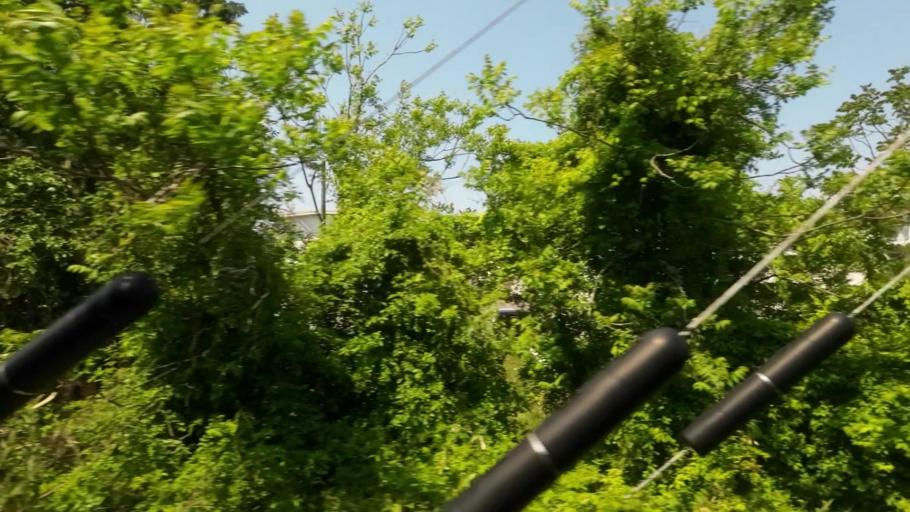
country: JP
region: Ehime
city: Hojo
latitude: 34.0712
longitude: 132.9324
